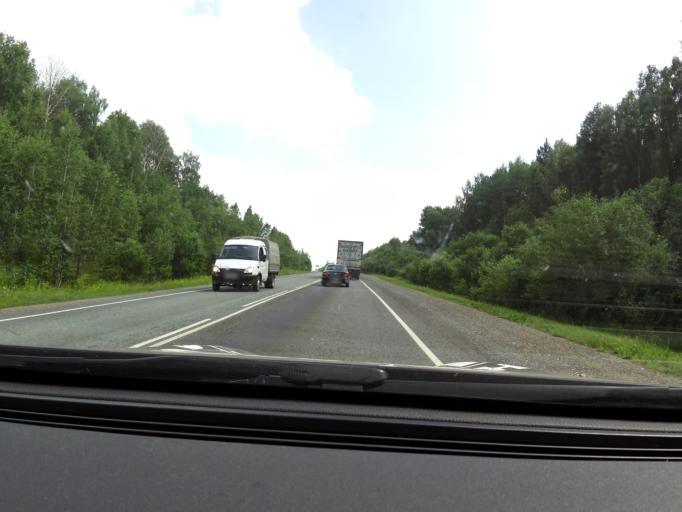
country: RU
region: Sverdlovsk
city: Achit
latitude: 56.8369
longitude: 57.7630
